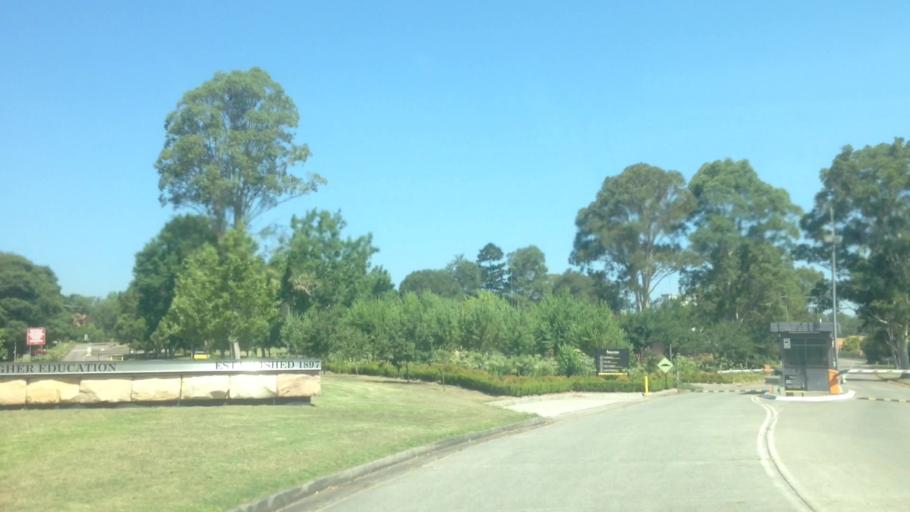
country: AU
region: New South Wales
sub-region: Lake Macquarie Shire
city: Cooranbong
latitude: -33.0843
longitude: 151.4591
